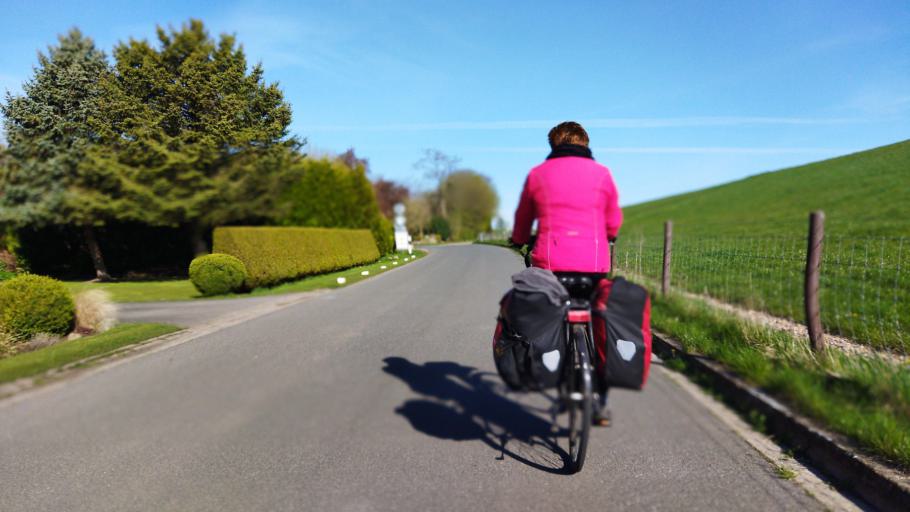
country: DE
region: Lower Saxony
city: Elsfleth
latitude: 53.2192
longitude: 8.4736
